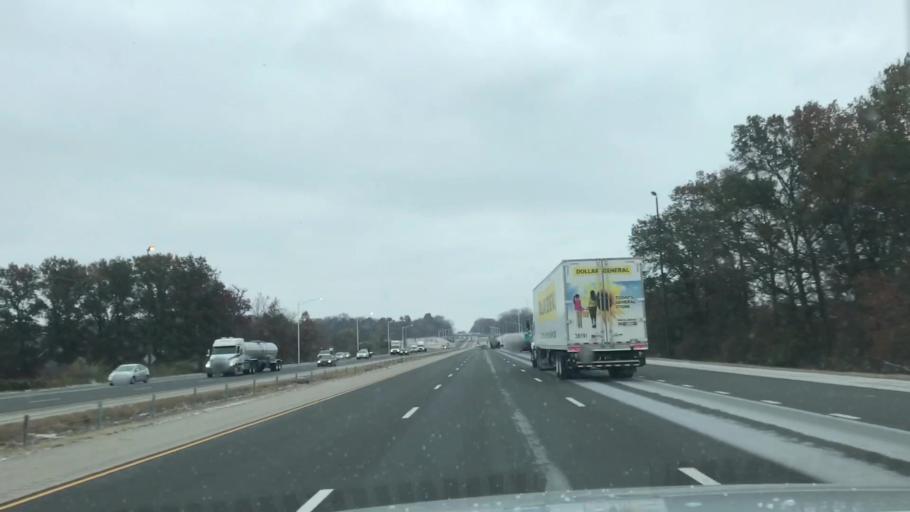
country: US
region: Illinois
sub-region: Madison County
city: Glen Carbon
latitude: 38.7567
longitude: -90.0187
